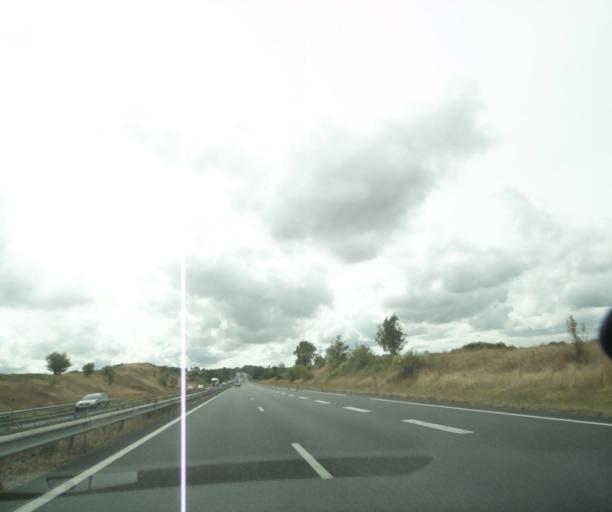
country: FR
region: Poitou-Charentes
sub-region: Departement de la Charente-Maritime
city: Mirambeau
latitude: 45.3662
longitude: -0.5901
